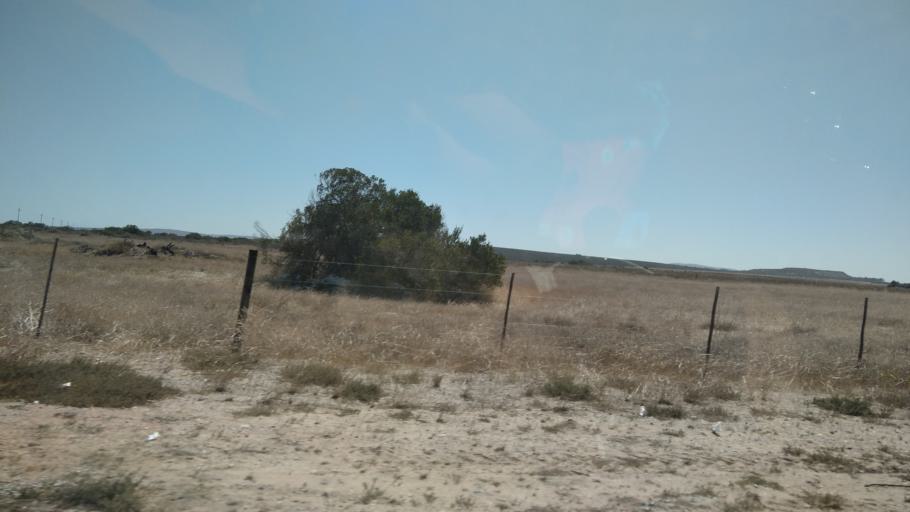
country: ZA
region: Western Cape
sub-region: West Coast District Municipality
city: Vredenburg
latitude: -32.9925
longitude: 18.1332
